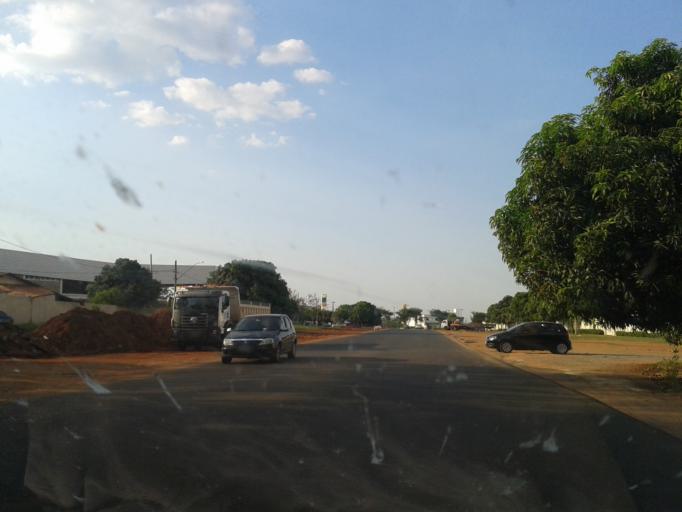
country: BR
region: Minas Gerais
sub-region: Uberlandia
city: Uberlandia
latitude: -18.9418
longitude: -48.3072
